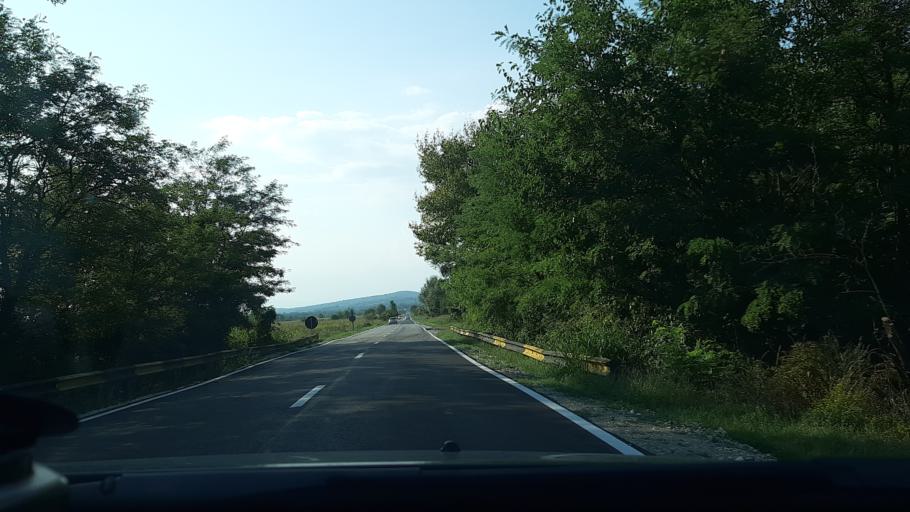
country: RO
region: Gorj
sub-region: Comuna Targu Carbunesti
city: Pojogeni
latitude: 45.0074
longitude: 23.4815
